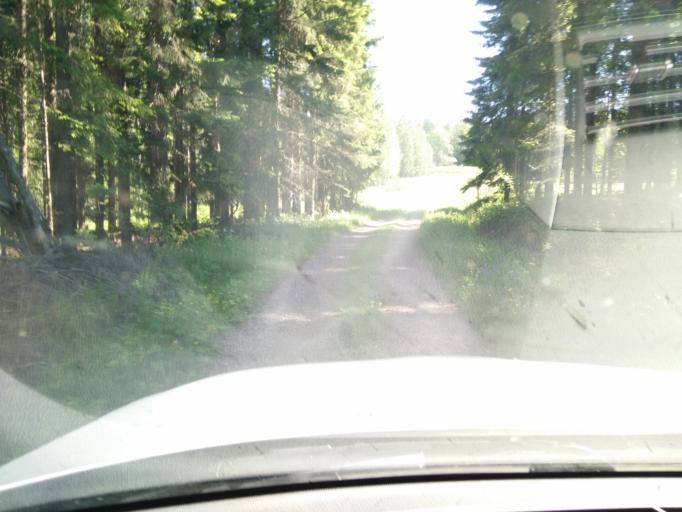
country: SE
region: Gaevleborg
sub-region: Hudiksvalls Kommun
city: Delsbo
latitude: 62.0575
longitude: 16.5904
